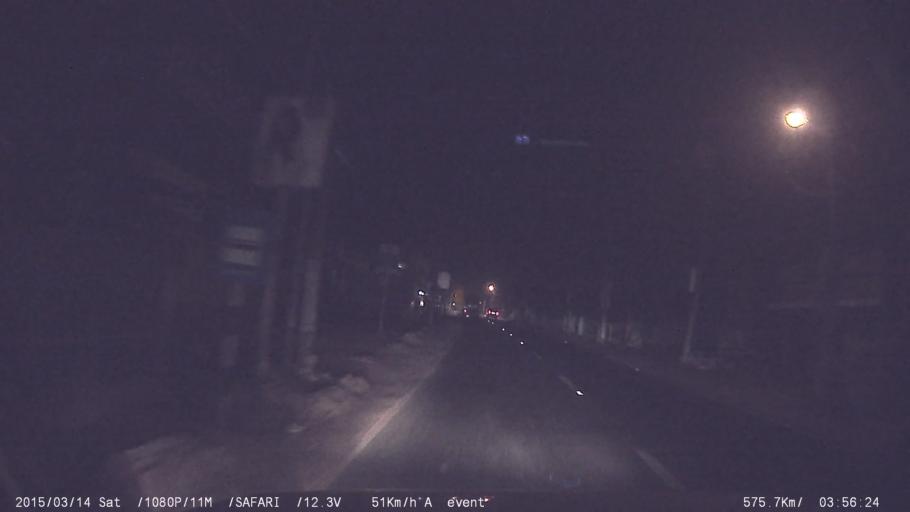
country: IN
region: Kerala
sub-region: Alappuzha
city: Alleppey
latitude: 9.4815
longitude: 76.3372
